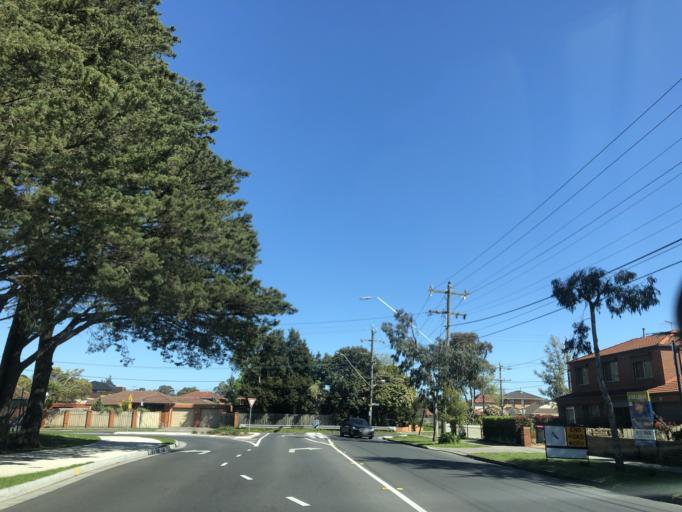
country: AU
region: Victoria
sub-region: Monash
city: Clayton
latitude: -37.9066
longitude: 145.1280
